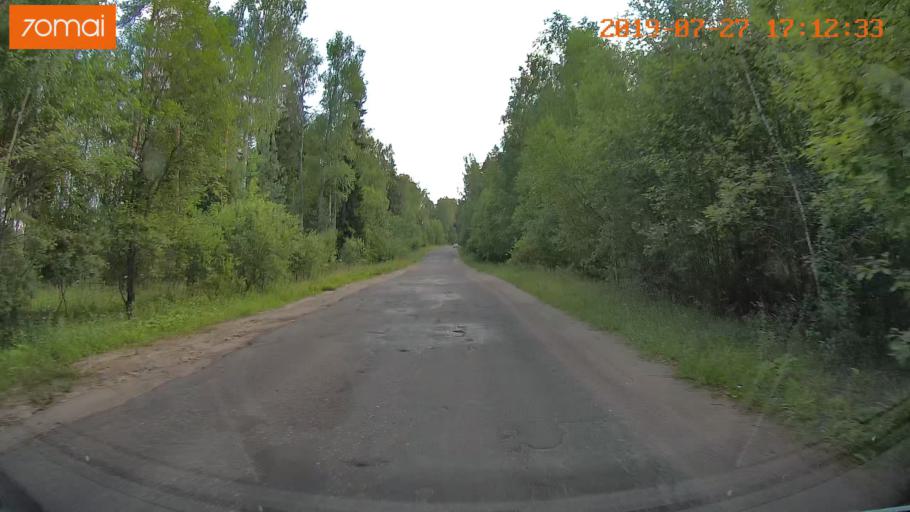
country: RU
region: Ivanovo
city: Novo-Talitsy
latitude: 57.0574
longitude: 40.8606
